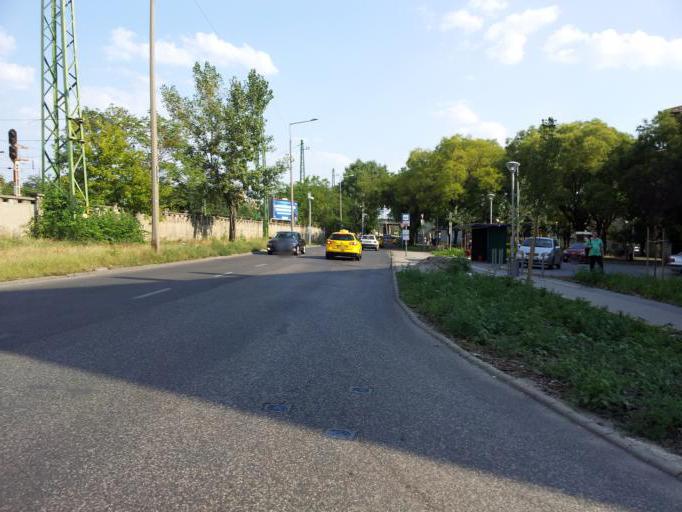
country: HU
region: Budapest
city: Budapest XIV. keruelet
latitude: 47.4911
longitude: 19.1207
